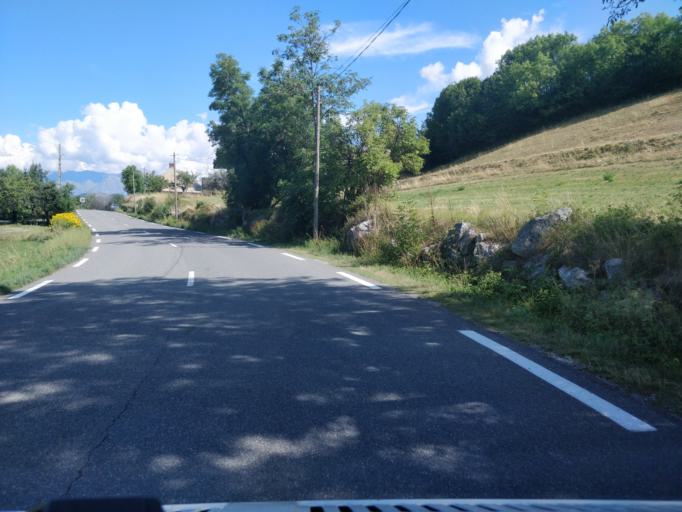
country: FR
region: Provence-Alpes-Cote d'Azur
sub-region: Departement des Alpes-de-Haute-Provence
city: Seyne-les-Alpes
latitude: 44.4160
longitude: 6.3517
